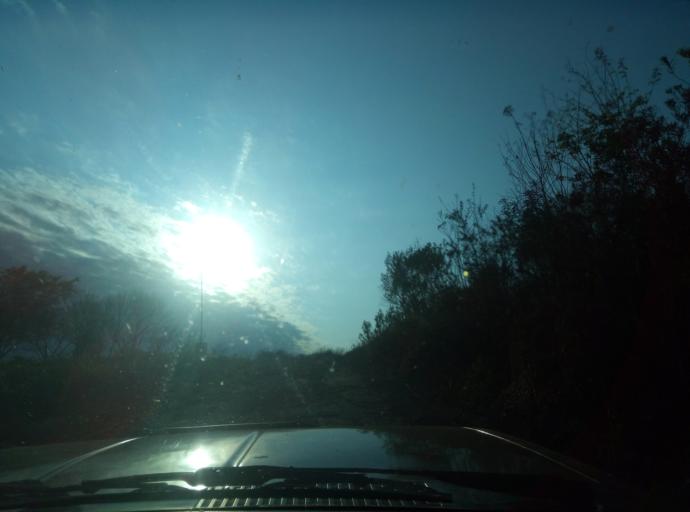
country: PY
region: Caaguazu
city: Doctor Cecilio Baez
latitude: -25.1989
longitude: -56.1183
